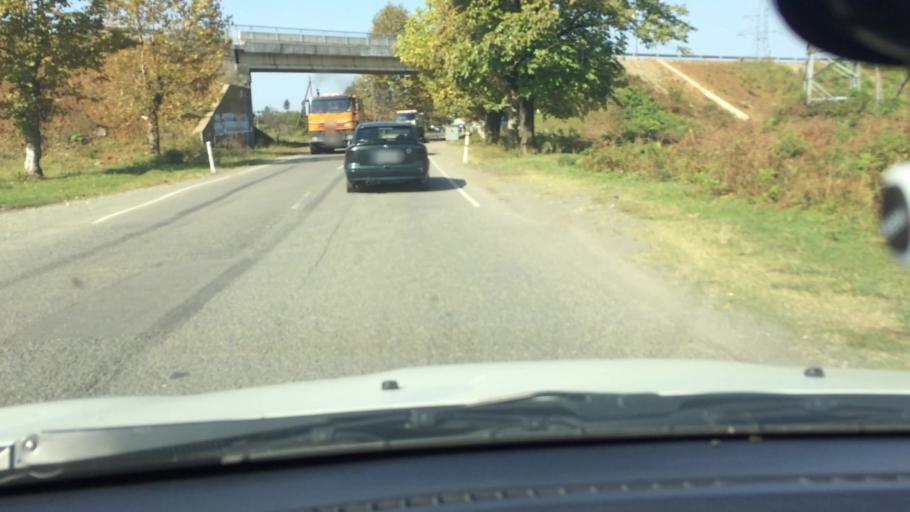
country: GE
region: Ajaria
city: Kobuleti
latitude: 41.8059
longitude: 41.7959
